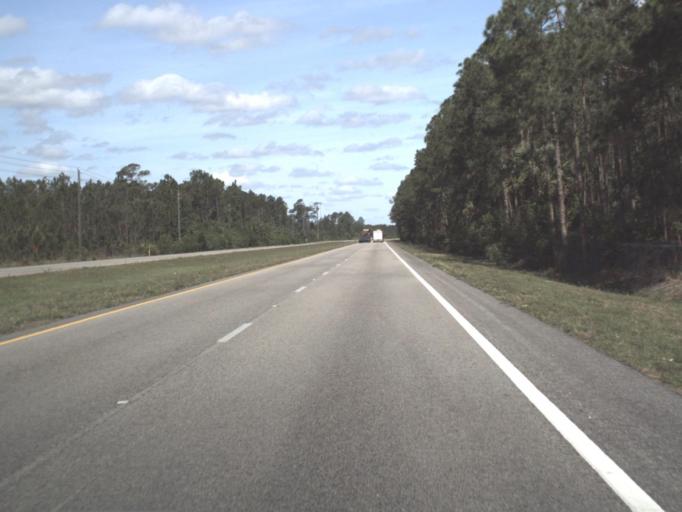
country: US
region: Florida
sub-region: Volusia County
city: Ormond-by-the-Sea
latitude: 29.3605
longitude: -81.1643
